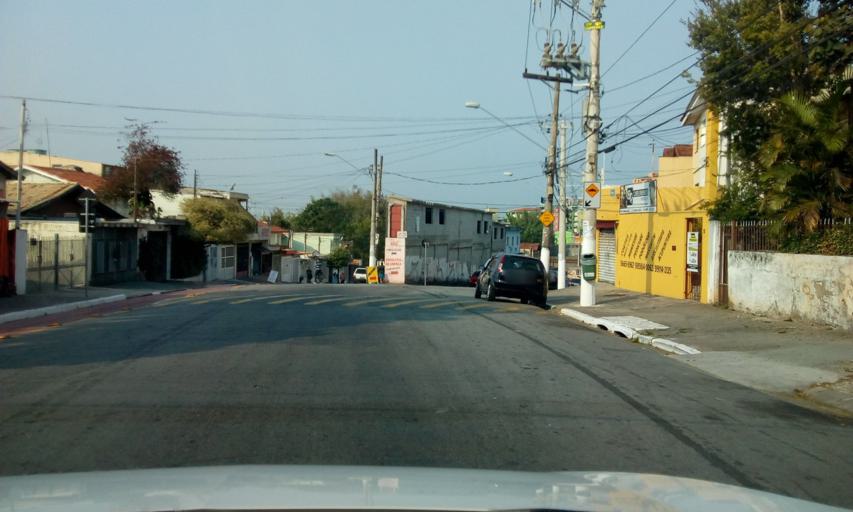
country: BR
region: Sao Paulo
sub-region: Diadema
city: Diadema
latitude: -23.7081
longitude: -46.6907
